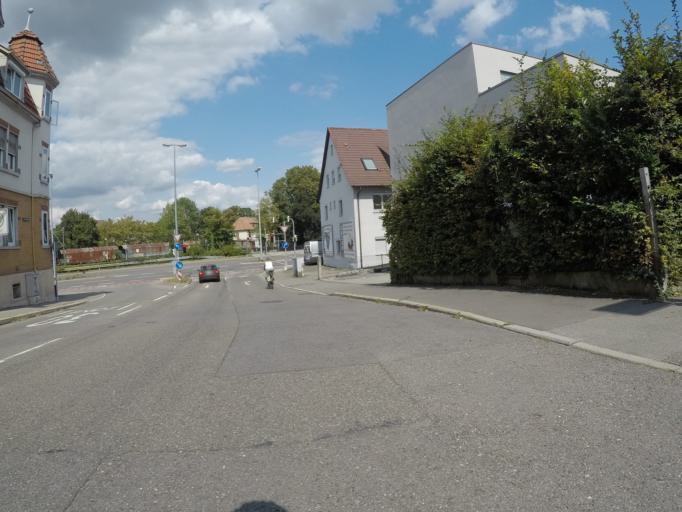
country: DE
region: Baden-Wuerttemberg
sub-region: Tuebingen Region
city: Reutlingen
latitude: 48.4919
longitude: 9.2017
